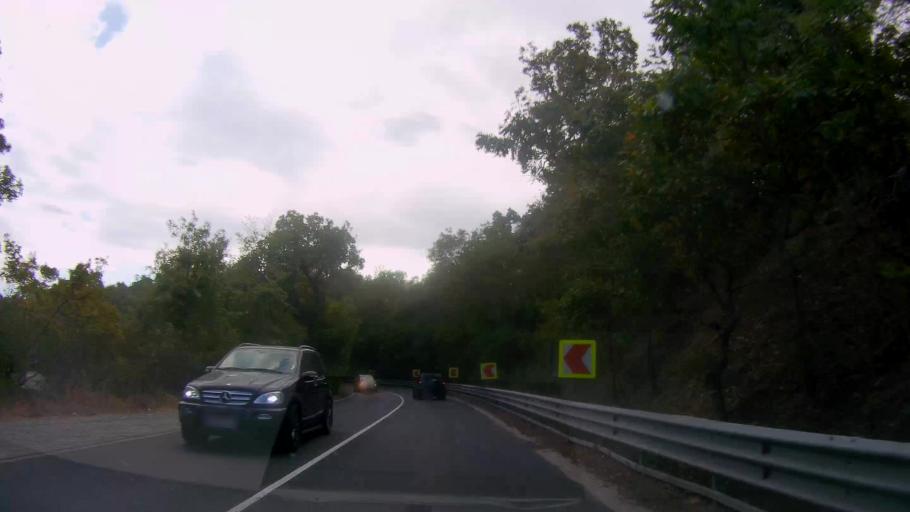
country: BG
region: Burgas
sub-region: Obshtina Primorsko
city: Primorsko
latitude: 42.3055
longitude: 27.7225
